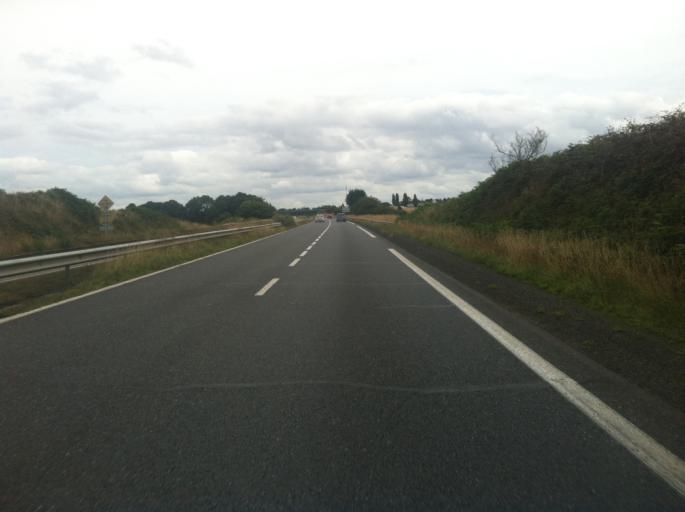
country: FR
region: Brittany
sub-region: Departement du Finistere
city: Saint-Thegonnec
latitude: 48.5271
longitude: -3.9485
